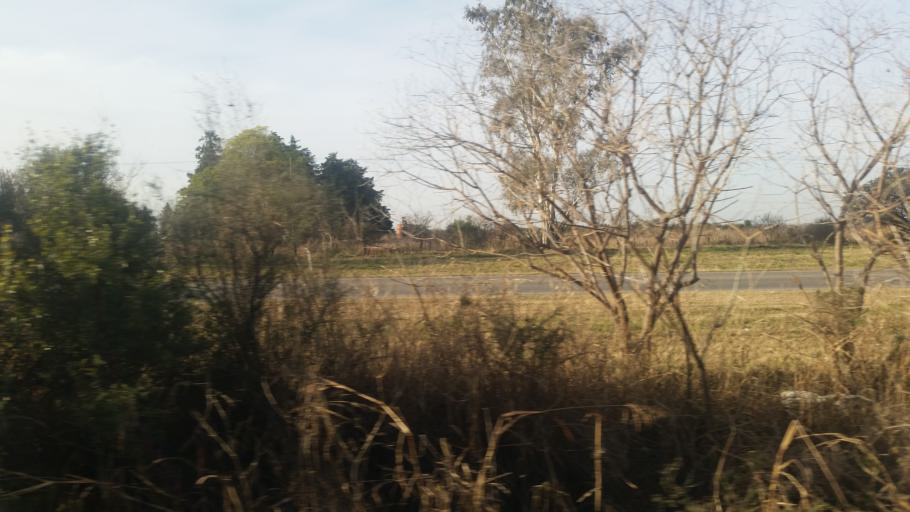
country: AR
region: Cordoba
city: Toledo
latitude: -31.5661
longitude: -63.9992
